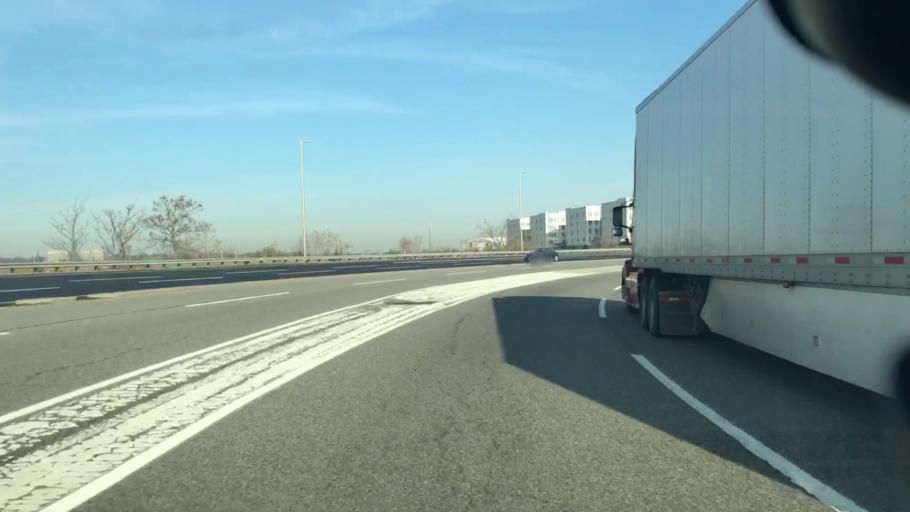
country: US
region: New Jersey
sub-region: Hudson County
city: Secaucus
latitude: 40.8052
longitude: -74.0811
